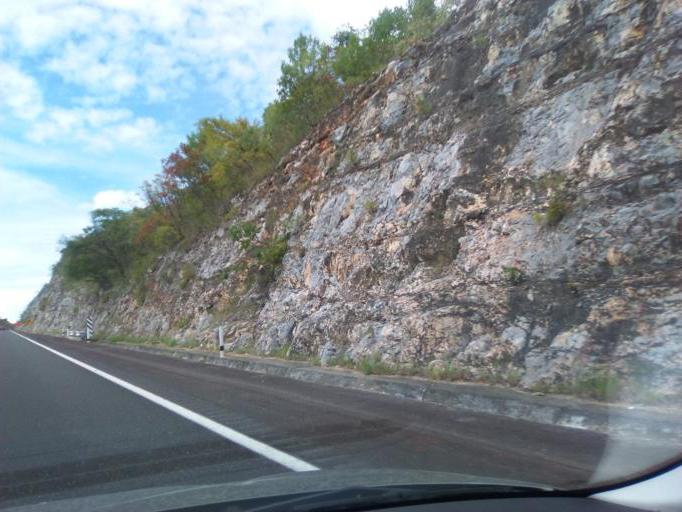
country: MX
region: Guerrero
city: Huitziltepec
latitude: 17.7844
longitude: -99.4837
